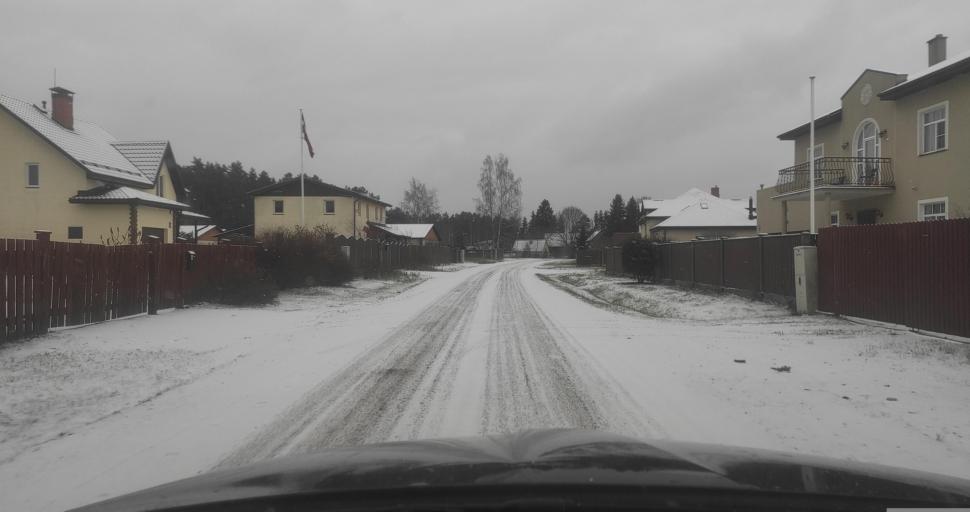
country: LV
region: Babite
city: Pinki
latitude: 56.9066
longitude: 23.8334
